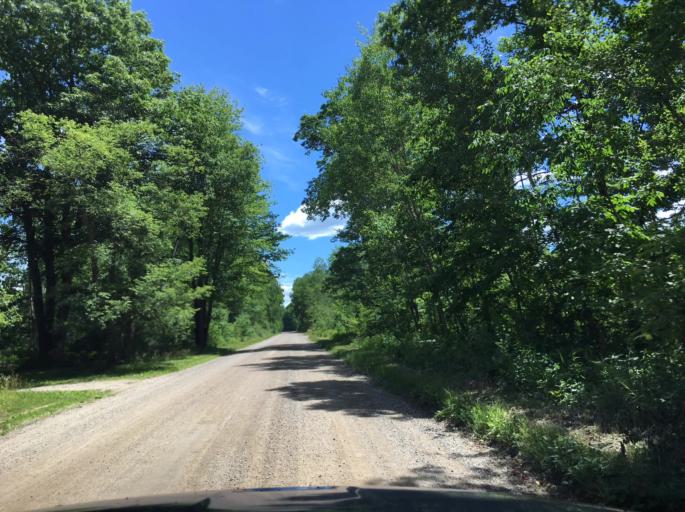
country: US
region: Michigan
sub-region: Osceola County
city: Evart
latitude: 43.8652
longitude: -85.3806
